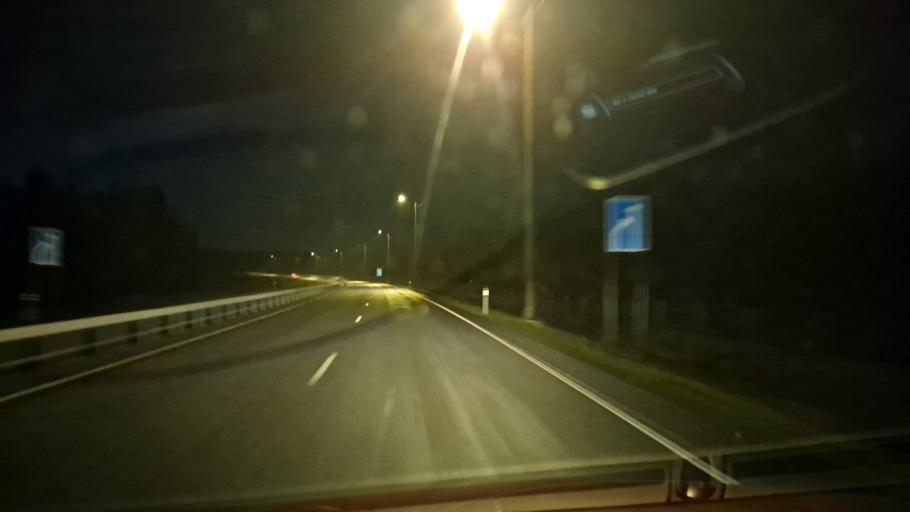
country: FI
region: Northern Ostrobothnia
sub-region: Oulunkaari
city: Kuivaniemi
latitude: 65.5587
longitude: 25.2375
